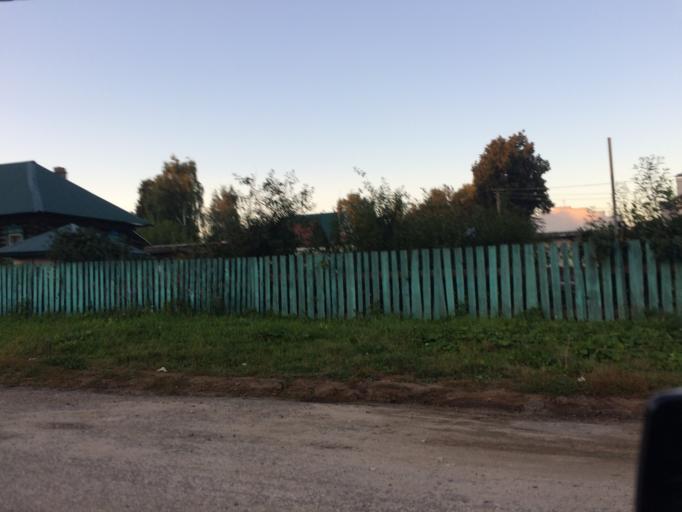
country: RU
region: Mariy-El
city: Yoshkar-Ola
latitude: 56.6434
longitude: 47.9077
